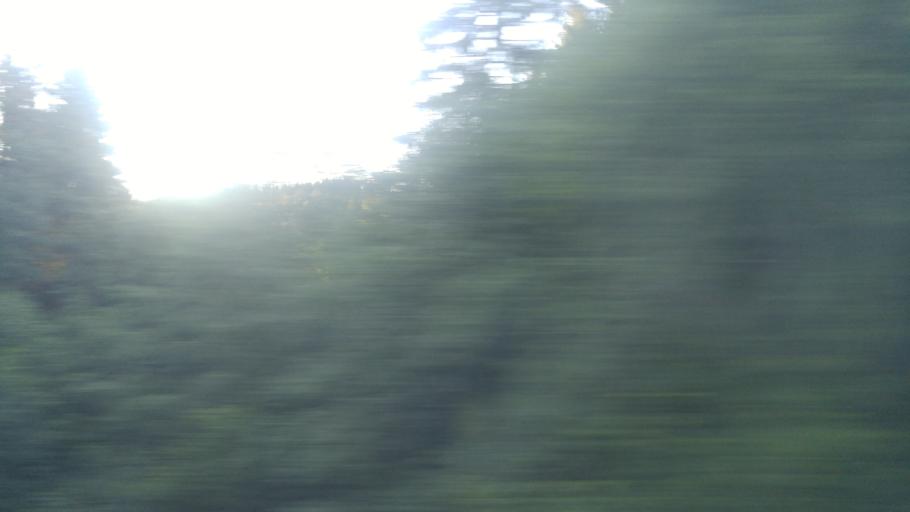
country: NO
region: Akershus
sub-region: Eidsvoll
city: Eidsvoll
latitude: 60.3155
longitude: 11.2379
